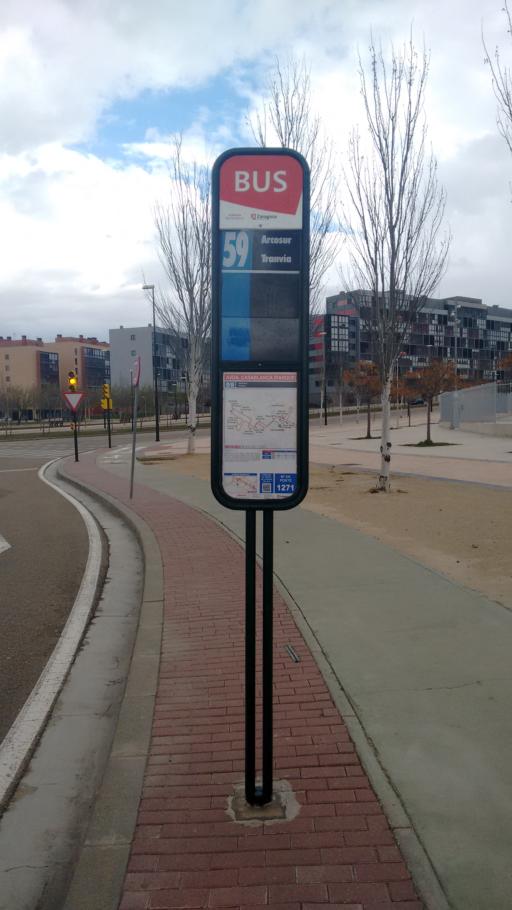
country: ES
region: Aragon
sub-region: Provincia de Zaragoza
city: Montecanal
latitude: 41.6215
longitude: -0.9358
